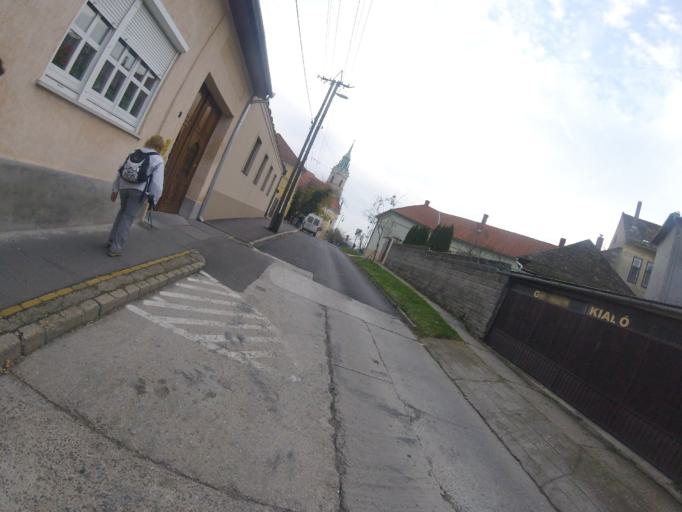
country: HU
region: Tolna
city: Szekszard
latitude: 46.3502
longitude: 18.6970
